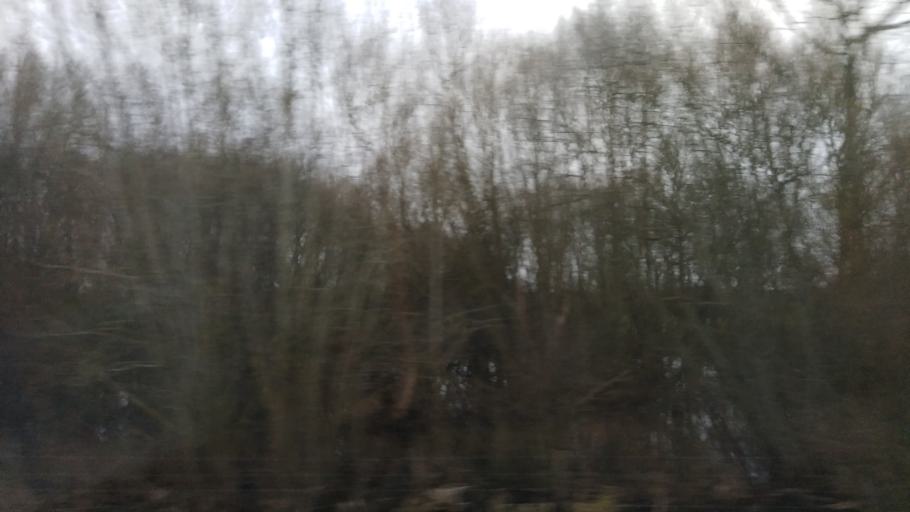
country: GB
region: England
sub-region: Kent
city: Staplehurst
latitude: 51.1735
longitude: 0.5221
